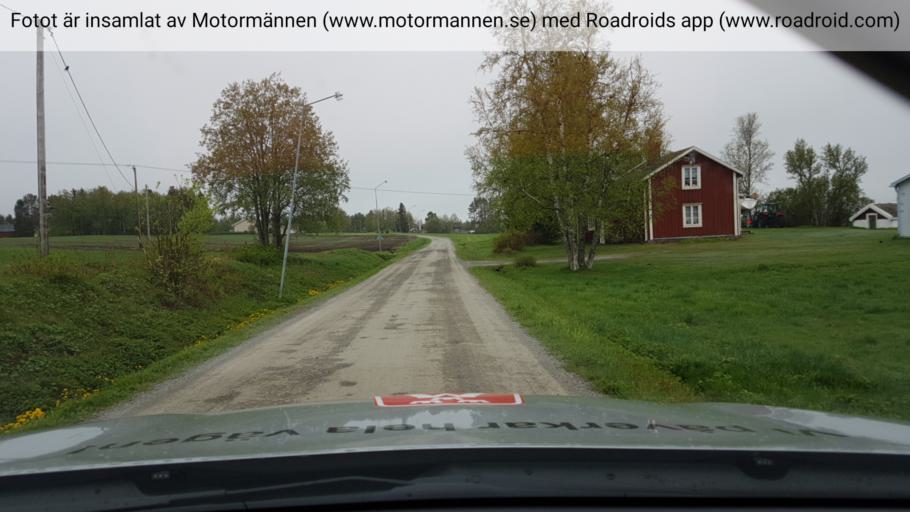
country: SE
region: Jaemtland
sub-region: Bergs Kommun
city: Hoverberg
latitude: 63.0260
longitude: 14.3728
